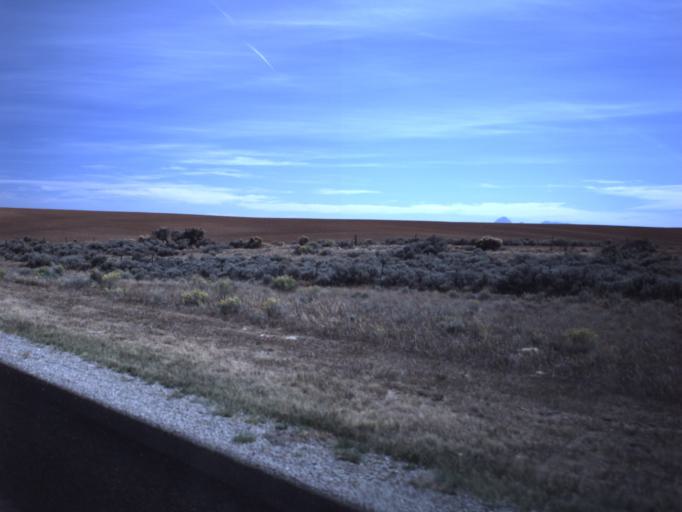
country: US
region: Colorado
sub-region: Dolores County
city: Dove Creek
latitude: 37.8185
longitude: -109.0491
